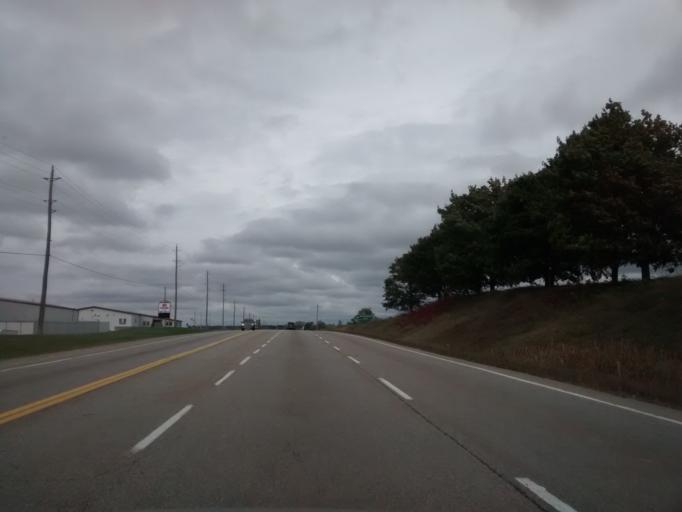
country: CA
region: Ontario
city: Ancaster
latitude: 43.0908
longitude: -79.9495
